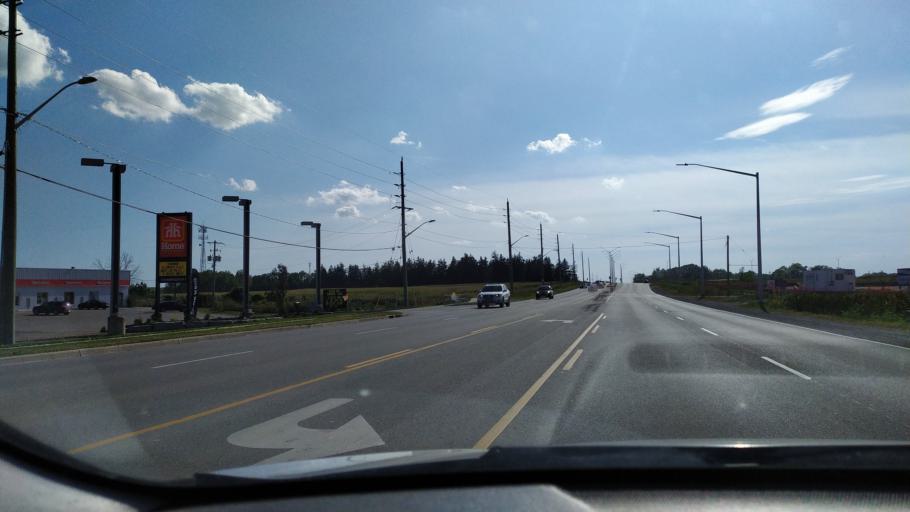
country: CA
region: Ontario
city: London
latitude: 42.9340
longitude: -81.2649
